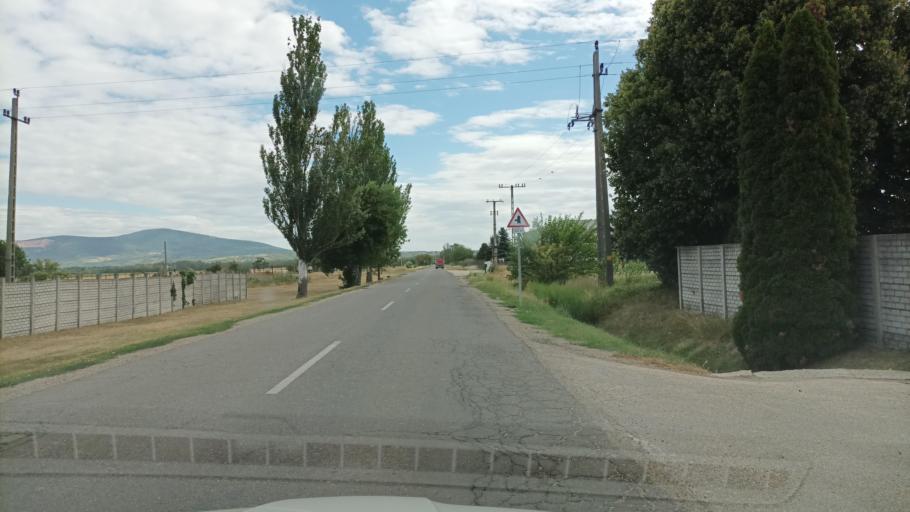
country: HU
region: Pest
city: Tahitotfalu
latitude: 47.7582
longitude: 19.0949
